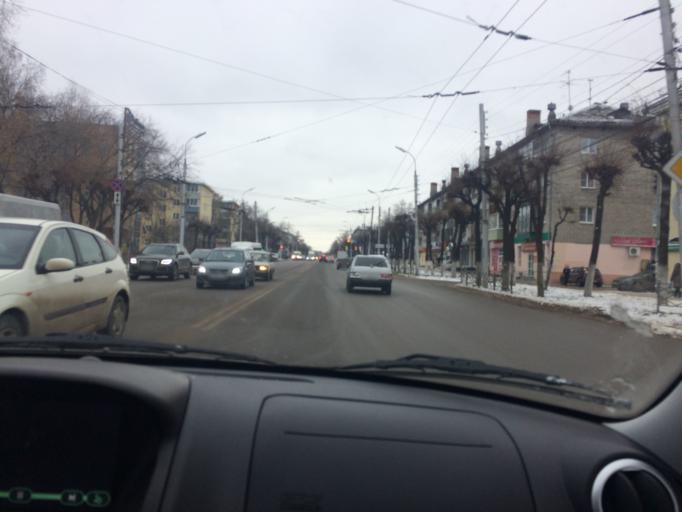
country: RU
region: Rjazan
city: Ryazan'
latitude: 54.6246
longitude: 39.7173
